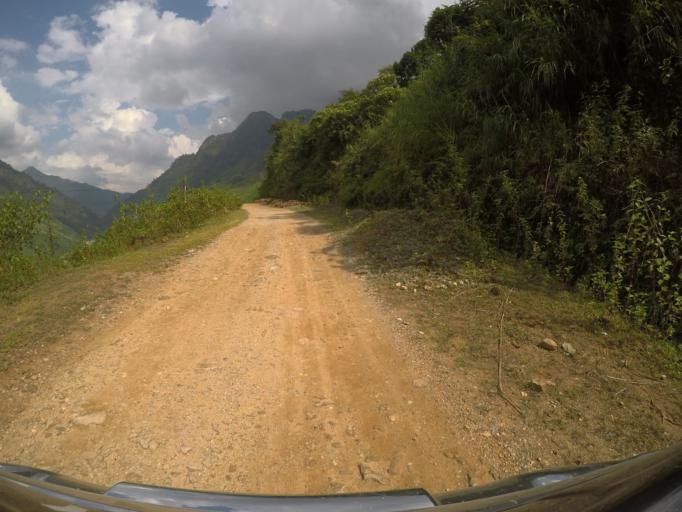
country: VN
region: Yen Bai
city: Son Thinh
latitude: 21.6795
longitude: 104.5482
